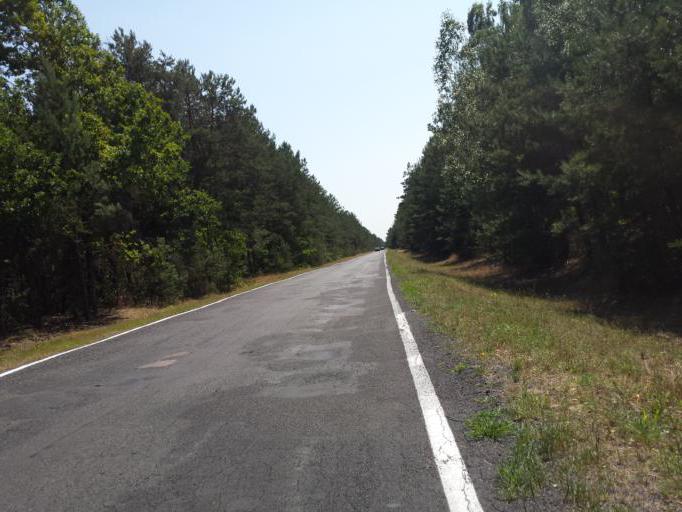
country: PL
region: Lublin Voivodeship
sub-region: Powiat bialski
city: Koden
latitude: 51.8669
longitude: 23.5957
